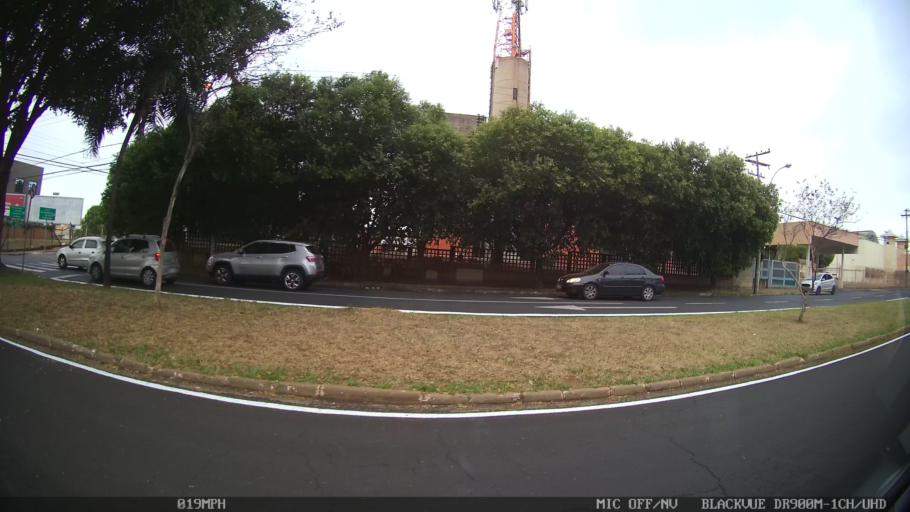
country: BR
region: Sao Paulo
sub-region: Sao Jose Do Rio Preto
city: Sao Jose do Rio Preto
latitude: -20.8336
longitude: -49.3972
